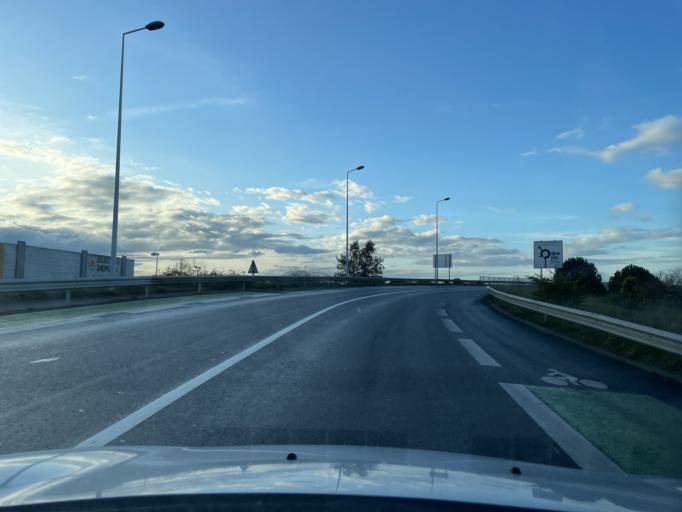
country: FR
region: Midi-Pyrenees
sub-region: Departement de la Haute-Garonne
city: Tournefeuille
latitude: 43.6053
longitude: 1.3064
